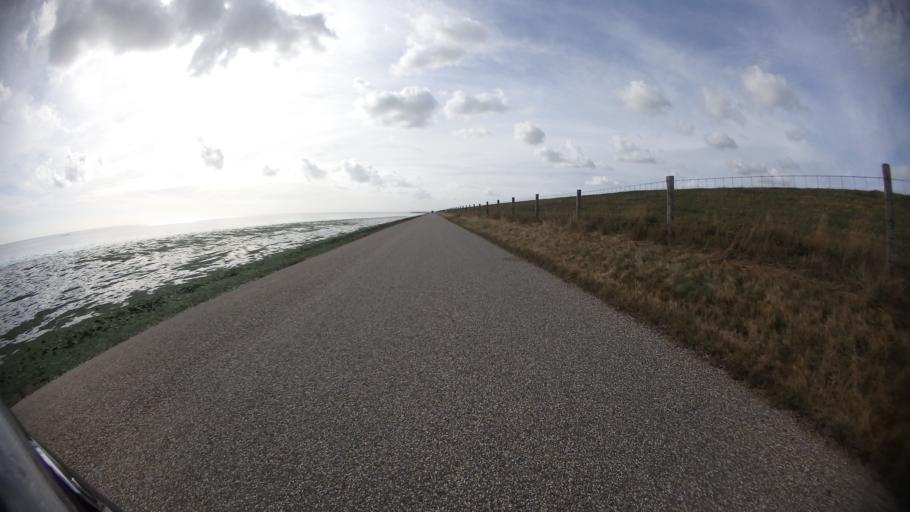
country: NL
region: North Holland
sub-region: Gemeente Texel
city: Den Burg
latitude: 53.1135
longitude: 4.8988
